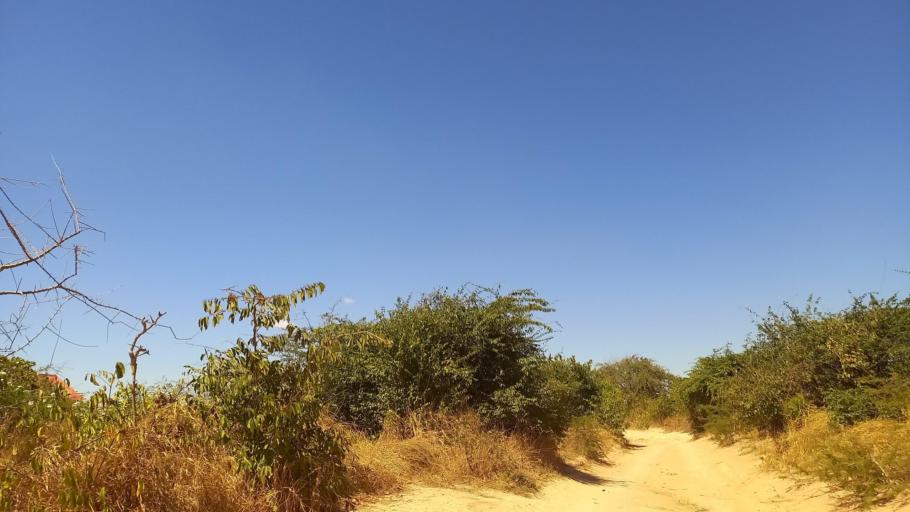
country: TZ
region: Dodoma
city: Dodoma
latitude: -6.1178
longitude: 35.6967
